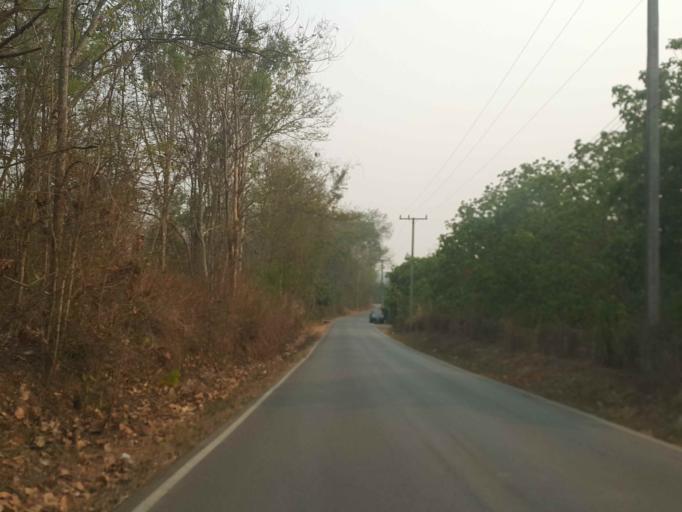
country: TH
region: Chiang Mai
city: Mae Taeng
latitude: 19.1071
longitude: 98.8990
